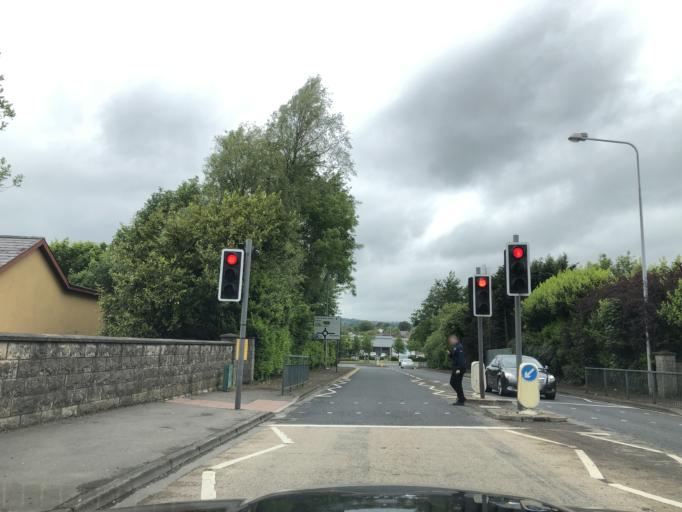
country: GB
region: Northern Ireland
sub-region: Lisburn District
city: Lisburn
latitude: 54.5142
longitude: -6.0540
